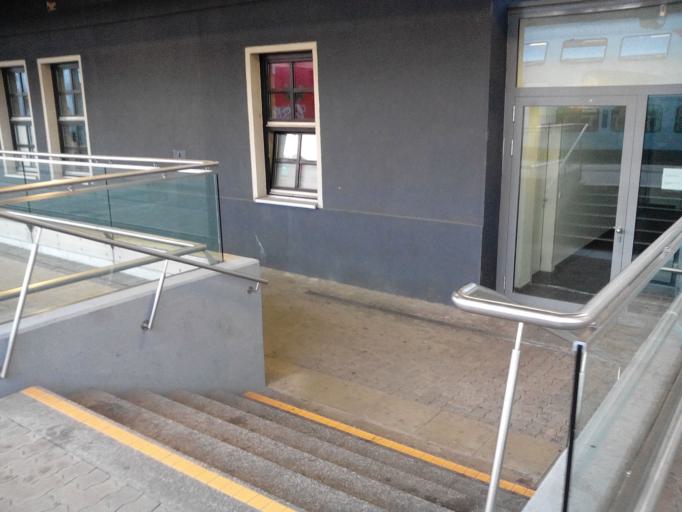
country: AT
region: Lower Austria
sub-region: Wiener Neustadt Stadt
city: Wiener Neustadt
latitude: 47.8127
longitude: 16.2336
